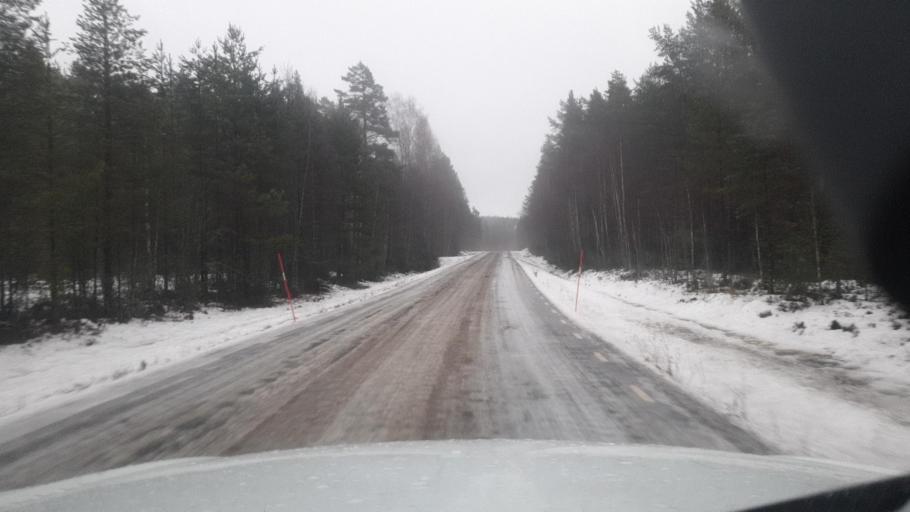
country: SE
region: Vaermland
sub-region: Torsby Kommun
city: Torsby
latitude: 59.9891
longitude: 12.7763
